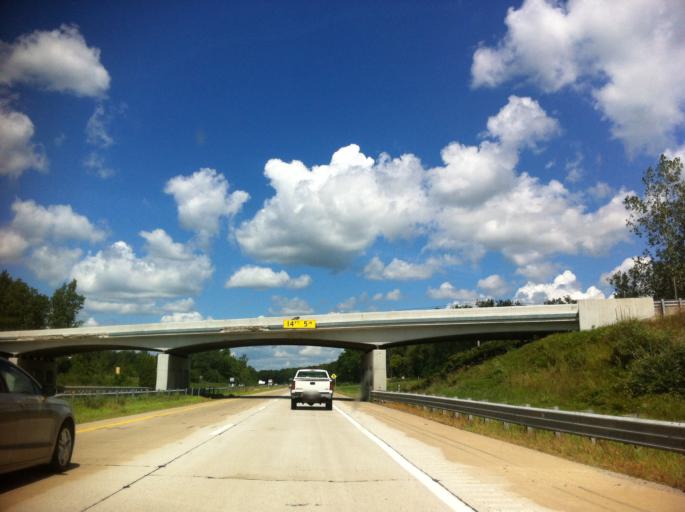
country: US
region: Michigan
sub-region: Monroe County
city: Petersburg
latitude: 41.8410
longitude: -83.6707
